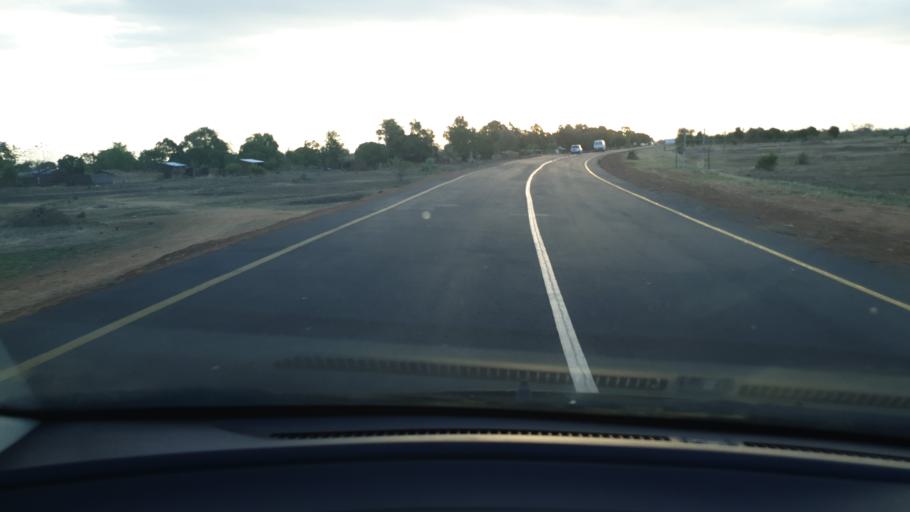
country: MW
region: Central Region
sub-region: Salima District
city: Salima
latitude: -13.7666
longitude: 34.5596
